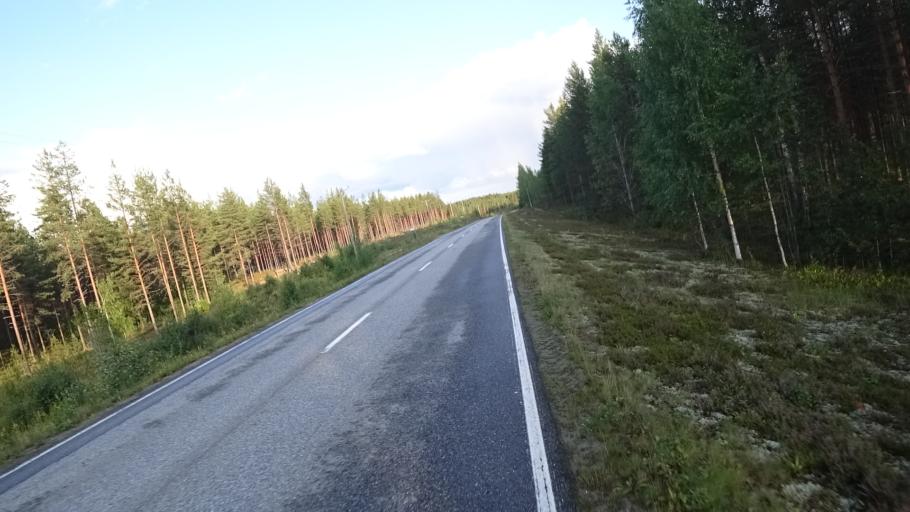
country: FI
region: North Karelia
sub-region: Joensuu
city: Ilomantsi
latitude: 62.6375
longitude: 31.0853
